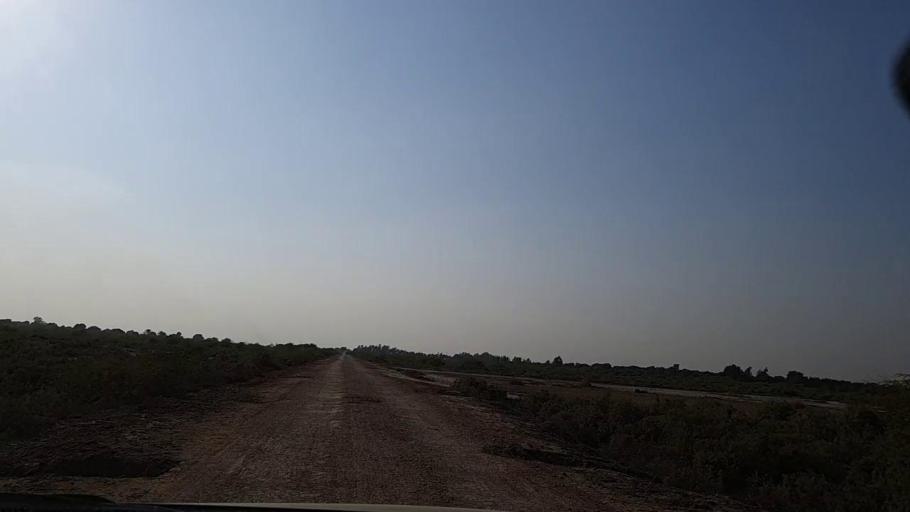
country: PK
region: Sindh
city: Mirwah Gorchani
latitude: 25.2240
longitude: 68.9685
